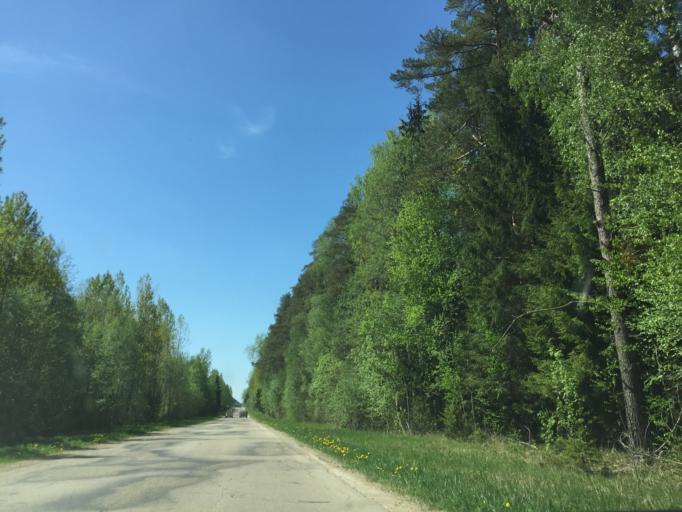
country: LV
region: Ogre
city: Ogre
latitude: 56.8525
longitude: 24.6902
